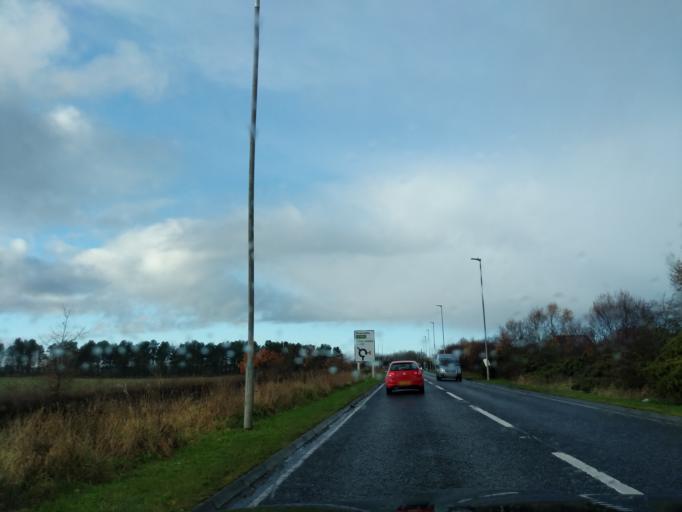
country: GB
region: England
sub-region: Northumberland
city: Seaton Delaval
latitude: 55.1033
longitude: -1.5379
